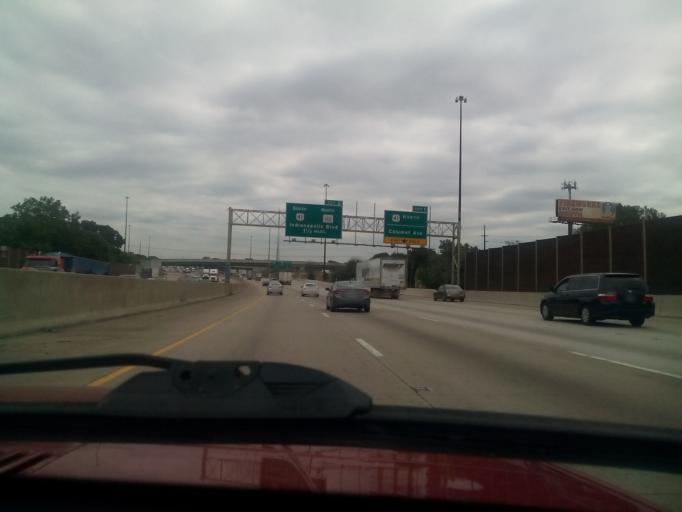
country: US
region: Indiana
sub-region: Lake County
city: Munster
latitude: 41.5744
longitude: -87.5153
